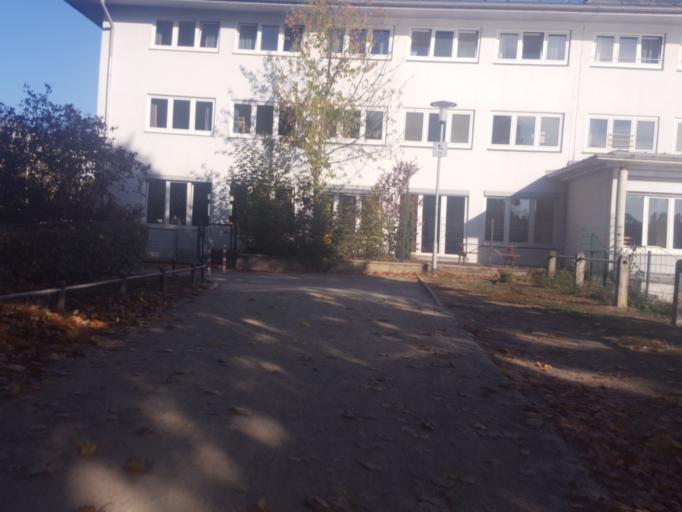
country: DE
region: Hesse
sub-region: Regierungsbezirk Darmstadt
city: Darmstadt
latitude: 49.8729
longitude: 8.6677
